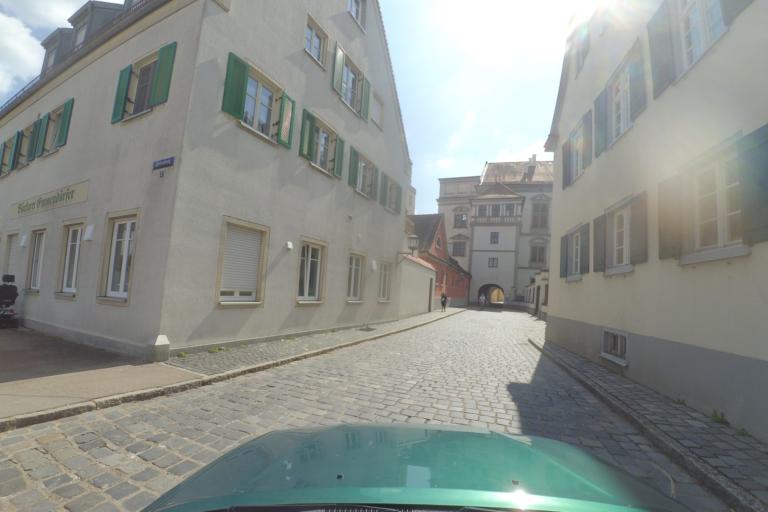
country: DE
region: Bavaria
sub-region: Swabia
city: Oettingen in Bayern
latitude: 48.9552
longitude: 10.6050
